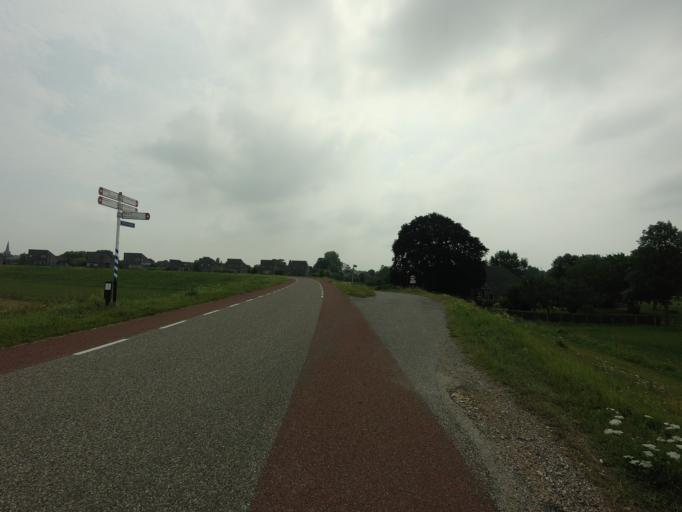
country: NL
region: Utrecht
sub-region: Gemeente Utrechtse Heuvelrug
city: Leersum
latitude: 51.9631
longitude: 5.4126
